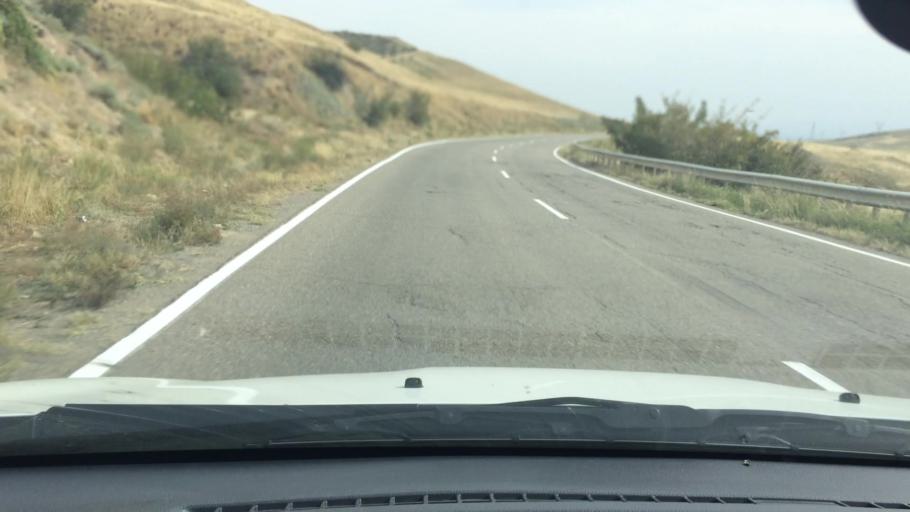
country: GE
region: Kvemo Kartli
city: Rust'avi
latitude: 41.4983
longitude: 44.9598
